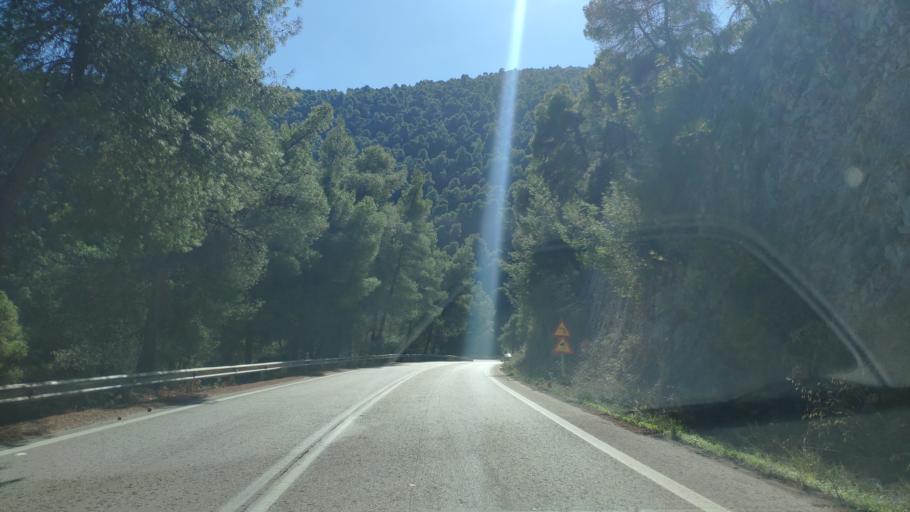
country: GR
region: Peloponnese
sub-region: Nomos Korinthias
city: Sofikon
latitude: 37.8241
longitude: 23.0826
